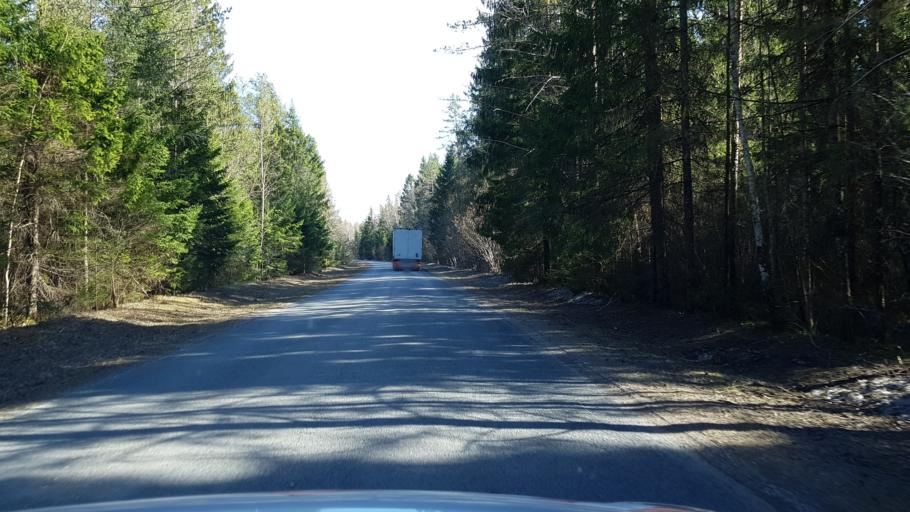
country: EE
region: Harju
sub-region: Nissi vald
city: Riisipere
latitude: 59.0916
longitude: 24.3444
